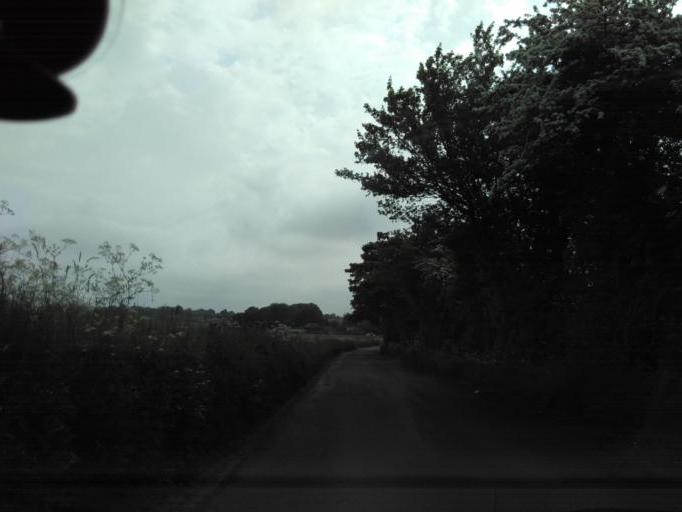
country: GB
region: England
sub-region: Kent
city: Canterbury
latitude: 51.2386
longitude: 1.0676
